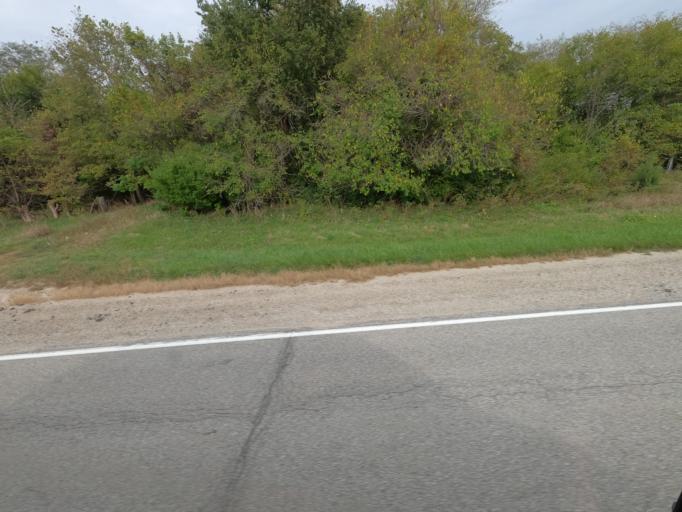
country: US
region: Iowa
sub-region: Van Buren County
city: Keosauqua
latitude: 40.8681
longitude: -92.1484
